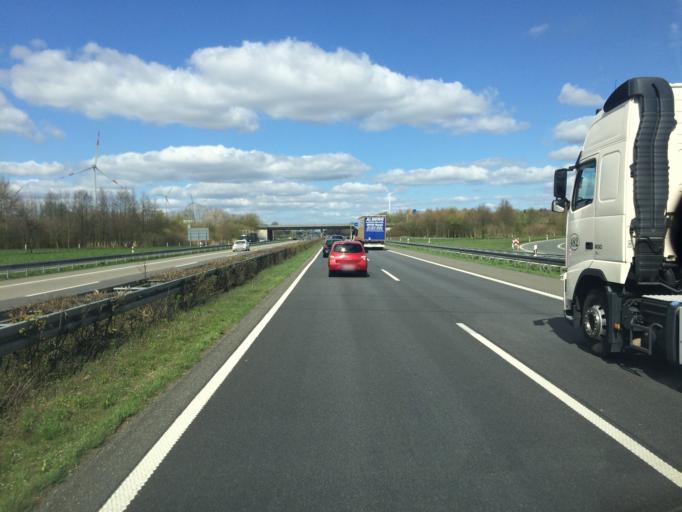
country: DE
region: North Rhine-Westphalia
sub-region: Regierungsbezirk Munster
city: Heek
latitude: 52.1893
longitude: 7.1143
